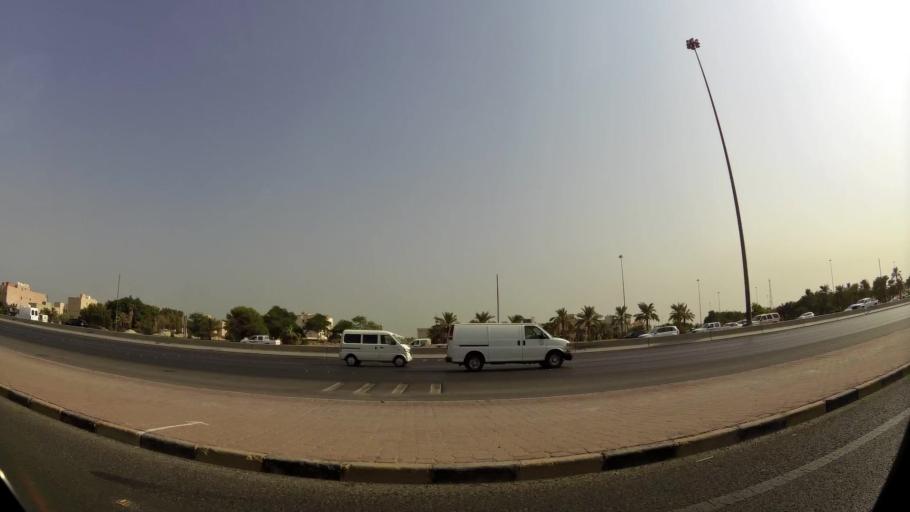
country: KW
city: Bayan
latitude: 29.3157
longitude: 48.0543
